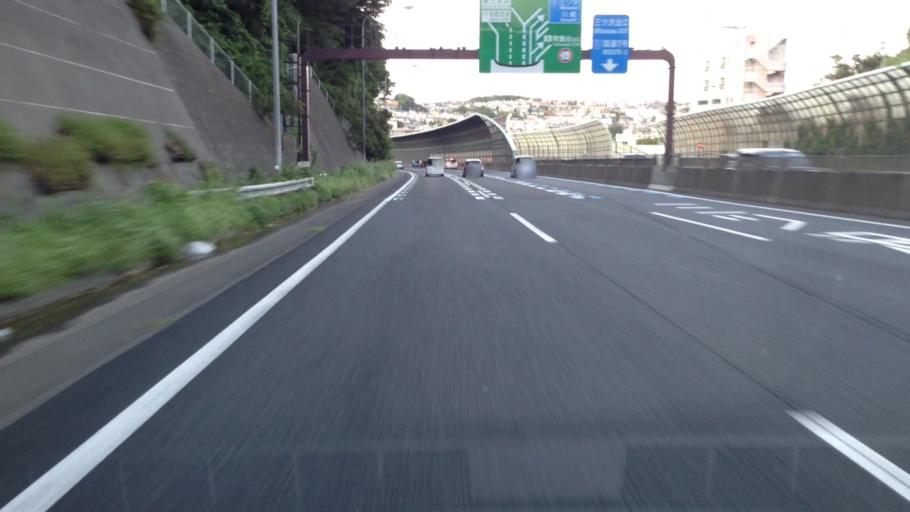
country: JP
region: Kanagawa
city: Yokohama
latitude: 35.4598
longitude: 139.5866
